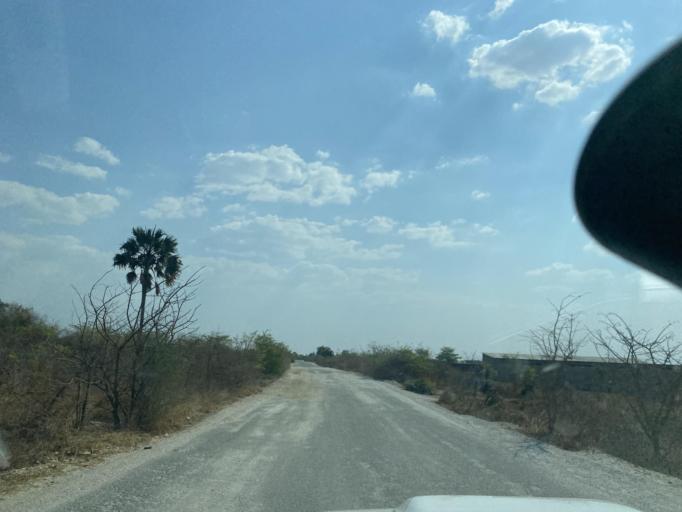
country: ZM
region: Lusaka
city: Lusaka
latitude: -15.3698
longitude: 28.0812
